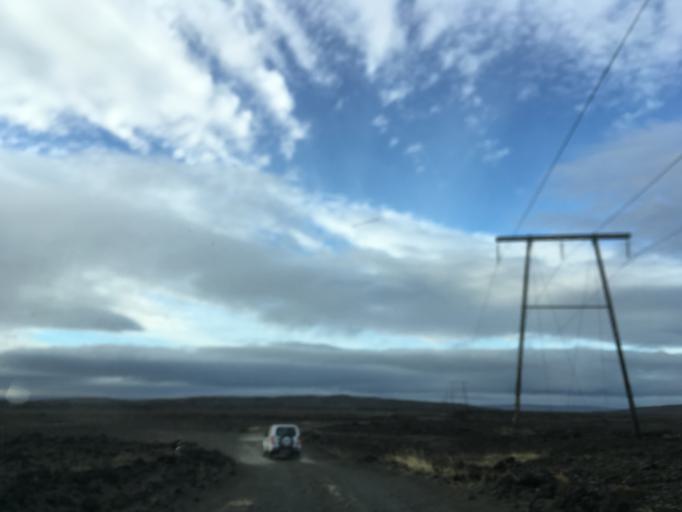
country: IS
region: South
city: Vestmannaeyjar
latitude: 64.1356
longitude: -19.1260
